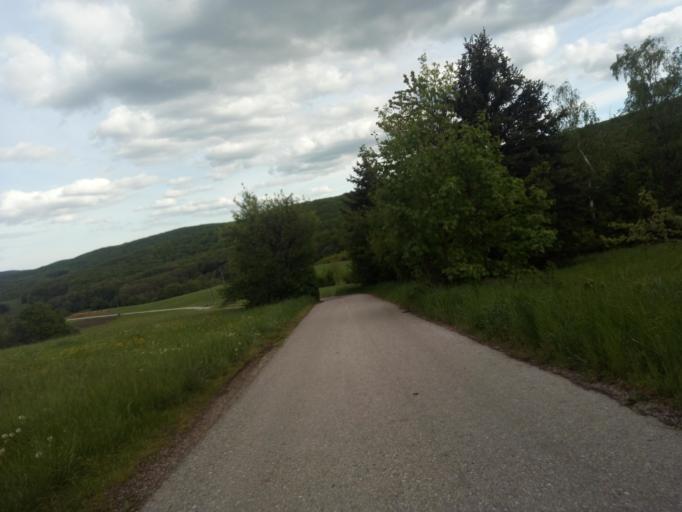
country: AT
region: Lower Austria
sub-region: Politischer Bezirk Modling
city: Breitenfurt bei Wien
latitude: 48.1354
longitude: 16.1284
